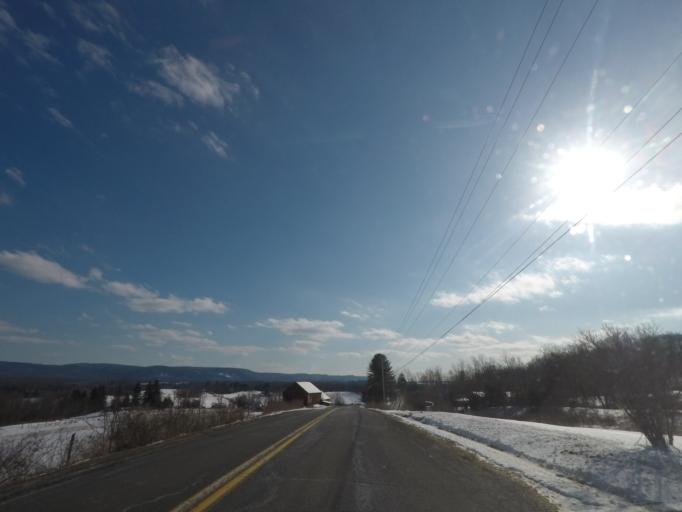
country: US
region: New York
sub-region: Rensselaer County
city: Hoosick Falls
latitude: 42.8572
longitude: -73.4993
